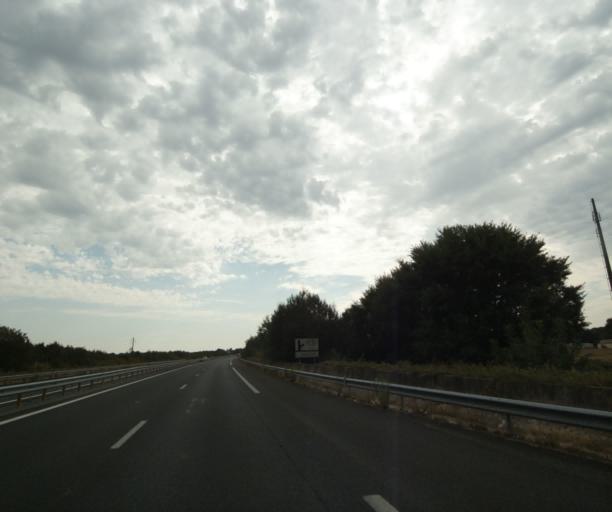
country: FR
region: Poitou-Charentes
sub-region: Departement de la Charente-Maritime
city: Tonnay-Charente
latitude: 45.9567
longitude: -0.9125
